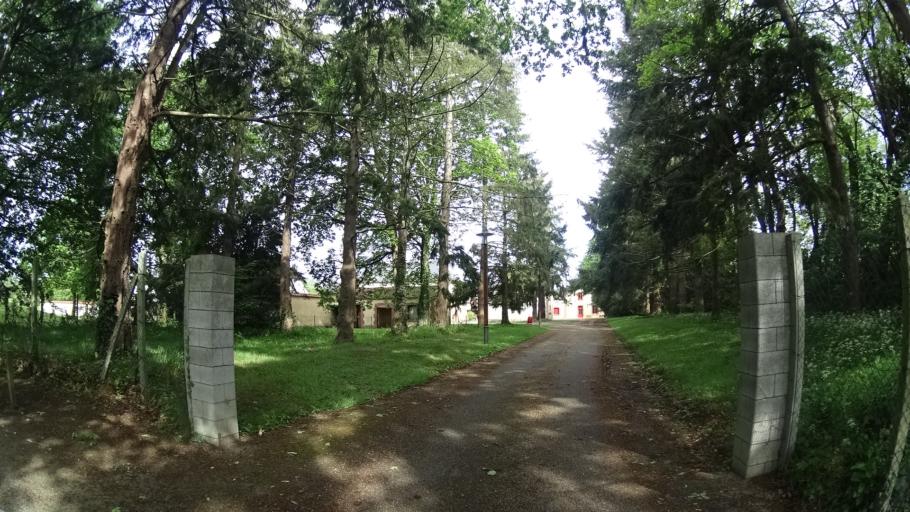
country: FR
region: Brittany
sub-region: Departement d'Ille-et-Vilaine
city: Mordelles
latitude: 48.0774
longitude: -1.8496
